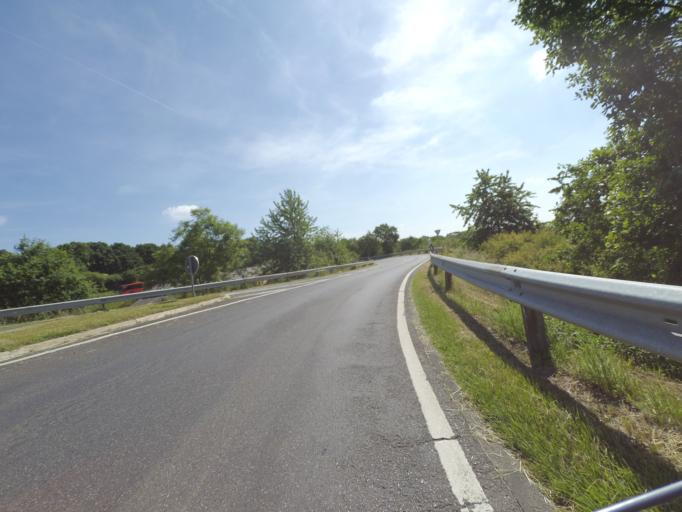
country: DE
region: Rheinland-Pfalz
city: Kaisersesch
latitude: 50.2276
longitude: 7.1440
